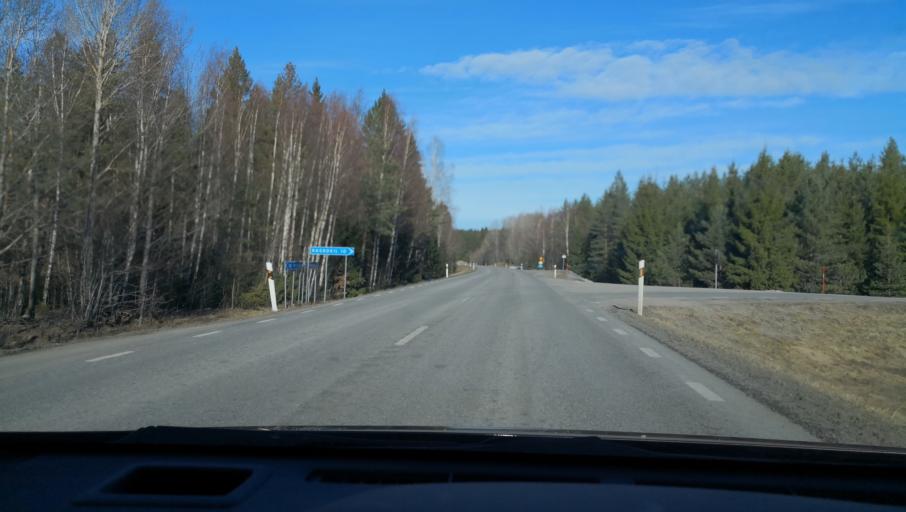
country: SE
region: Uppsala
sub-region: Uppsala Kommun
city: Vattholma
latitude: 60.0243
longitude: 17.7480
